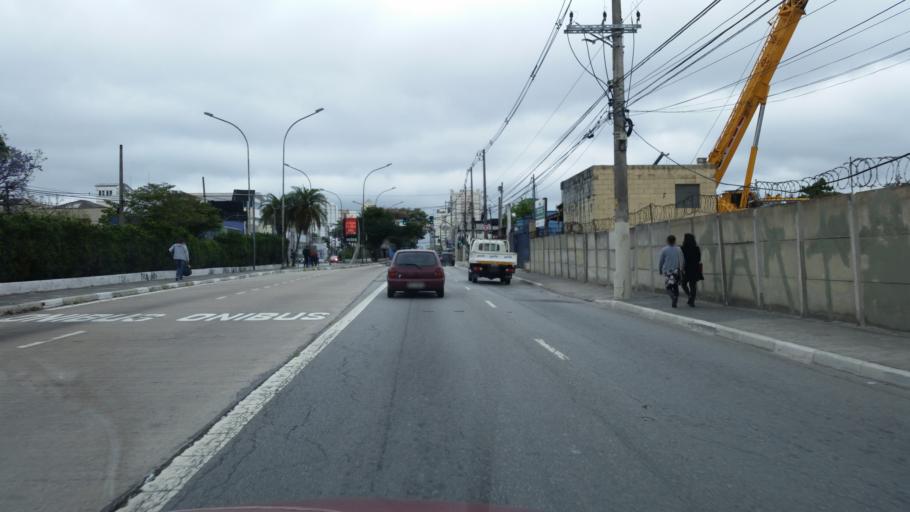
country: BR
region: Sao Paulo
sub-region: Sao Paulo
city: Sao Paulo
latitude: -23.6097
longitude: -46.6681
